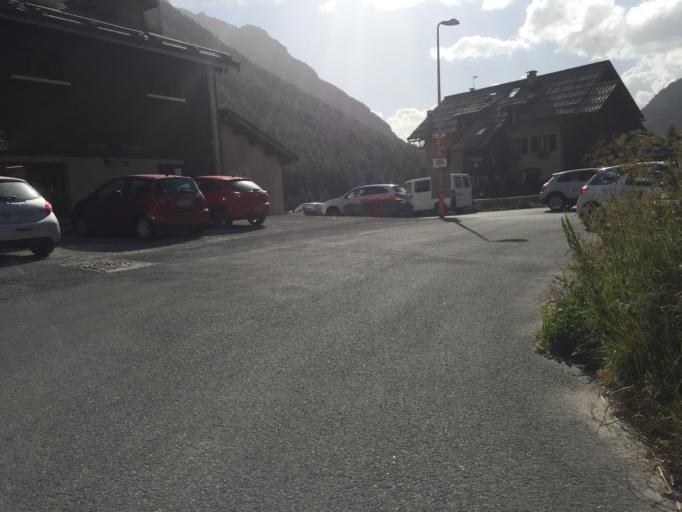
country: FR
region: Provence-Alpes-Cote d'Azur
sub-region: Departement des Hautes-Alpes
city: Guillestre
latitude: 44.6661
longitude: 6.7764
